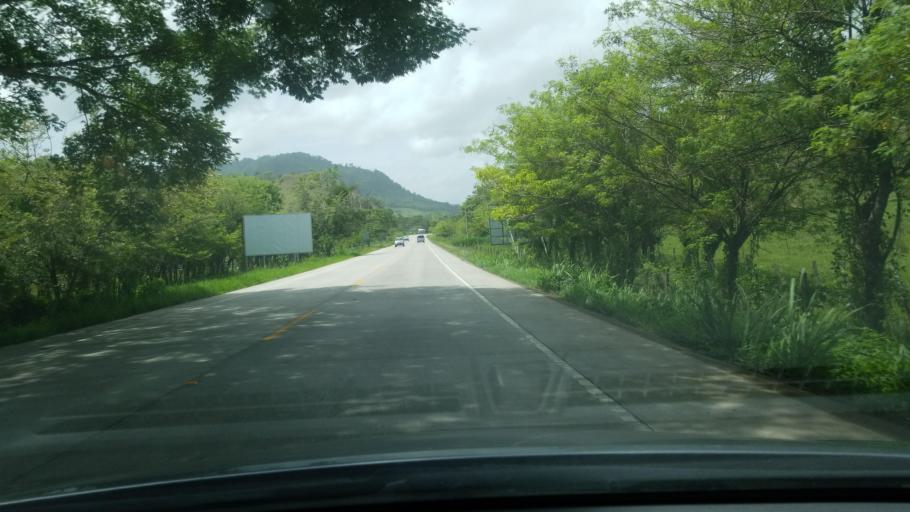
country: HN
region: Copan
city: Trinidad de Copan
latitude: 14.9606
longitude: -88.7720
